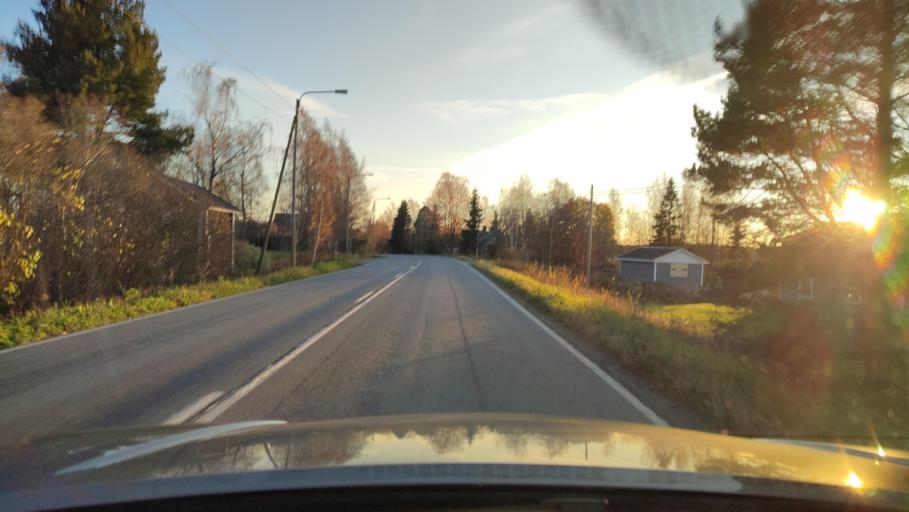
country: FI
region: Ostrobothnia
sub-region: Sydosterbotten
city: Naerpes
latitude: 62.4957
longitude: 21.3444
